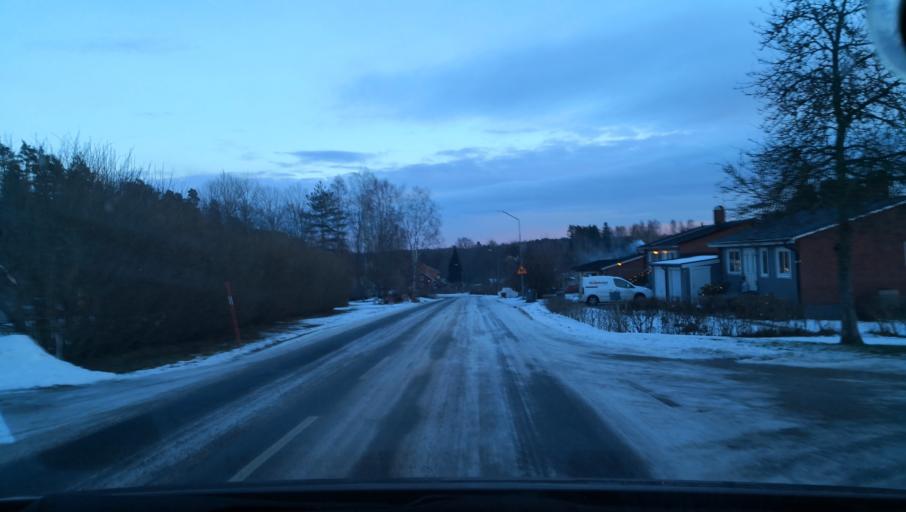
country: SE
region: Soedermanland
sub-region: Katrineholms Kommun
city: Katrineholm
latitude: 59.0912
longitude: 16.2036
